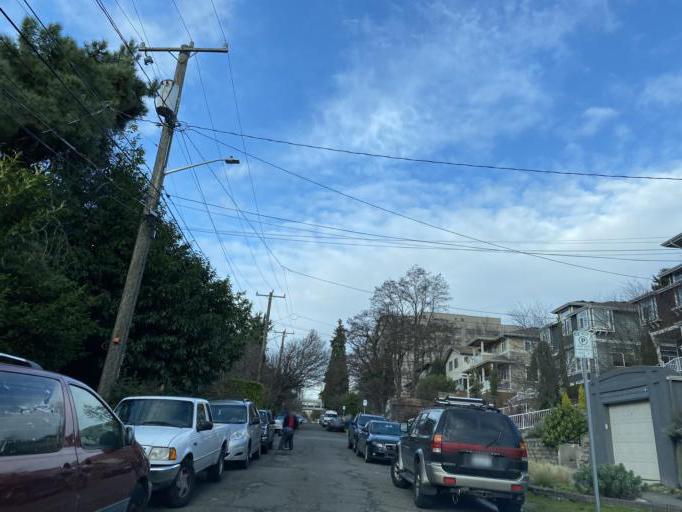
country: US
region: Washington
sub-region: King County
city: Seattle
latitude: 47.6049
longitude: -122.3116
